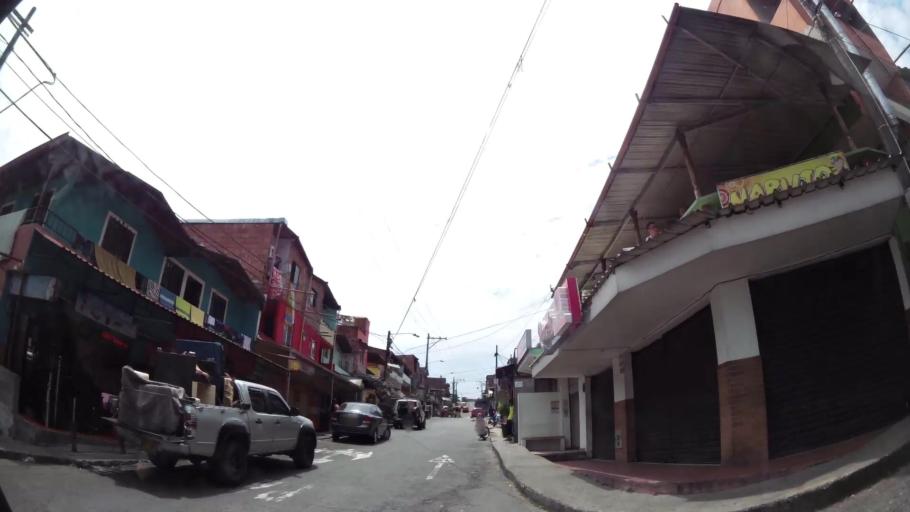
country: CO
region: Antioquia
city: Bello
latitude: 6.3123
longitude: -75.5793
